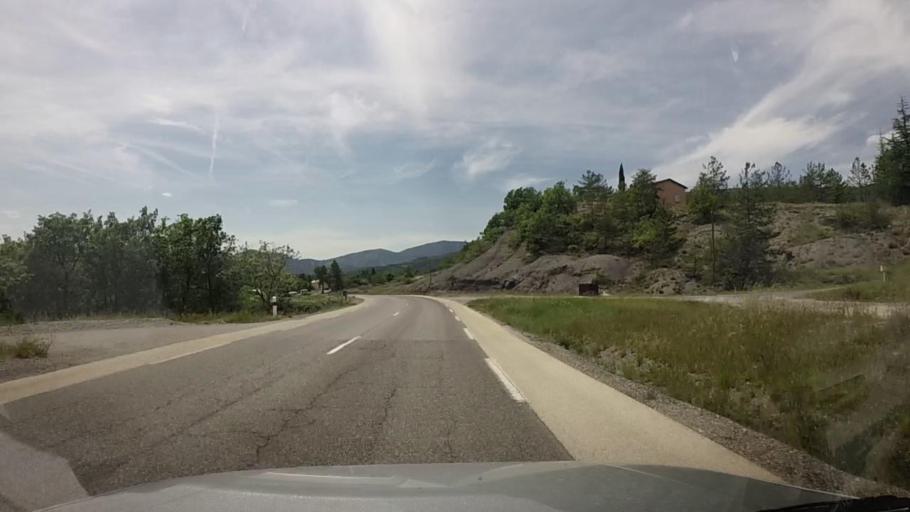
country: FR
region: Provence-Alpes-Cote d'Azur
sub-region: Departement des Alpes-de-Haute-Provence
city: Le Brusquet
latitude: 44.1569
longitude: 6.3001
